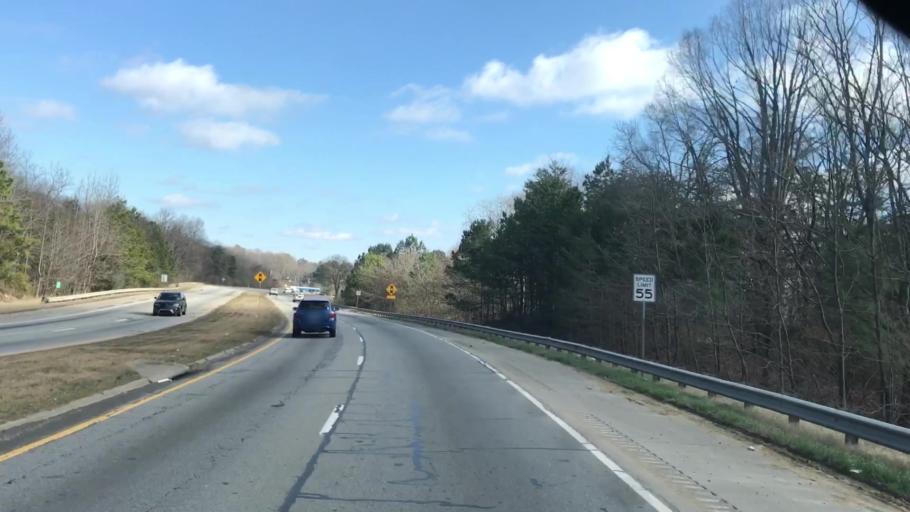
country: US
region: Georgia
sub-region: Hall County
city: Gainesville
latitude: 34.2815
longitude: -83.7965
